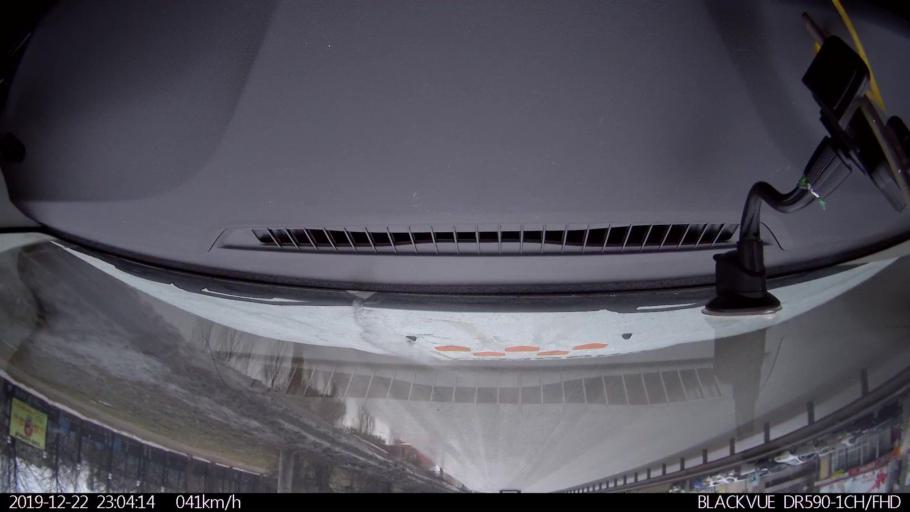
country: RU
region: Nizjnij Novgorod
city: Gorbatovka
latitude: 56.2550
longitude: 43.8530
